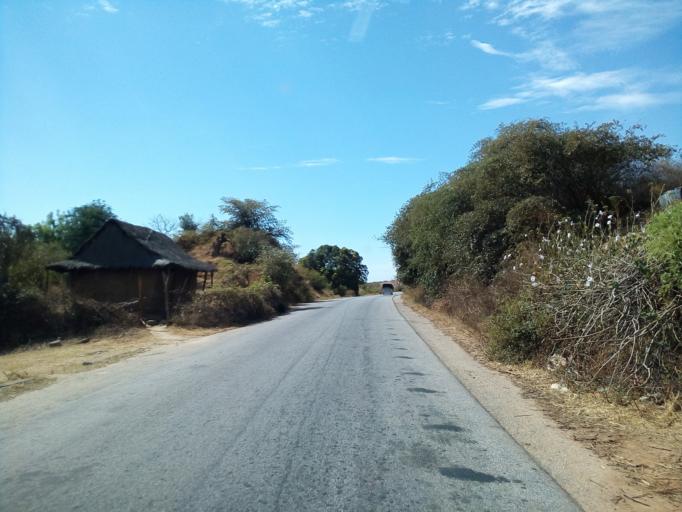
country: MG
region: Betsiboka
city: Maevatanana
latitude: -16.9197
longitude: 46.8676
